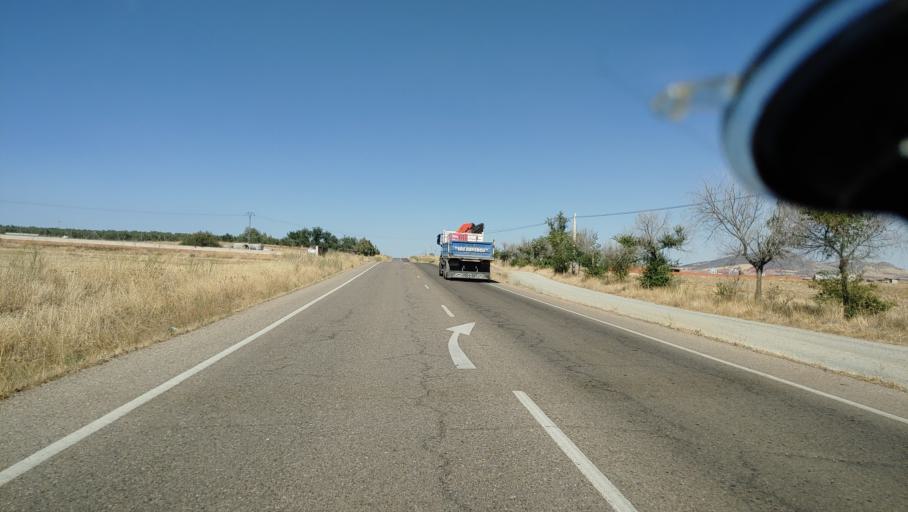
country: ES
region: Castille-La Mancha
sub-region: Province of Toledo
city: Pulgar
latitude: 39.7019
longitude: -4.1442
